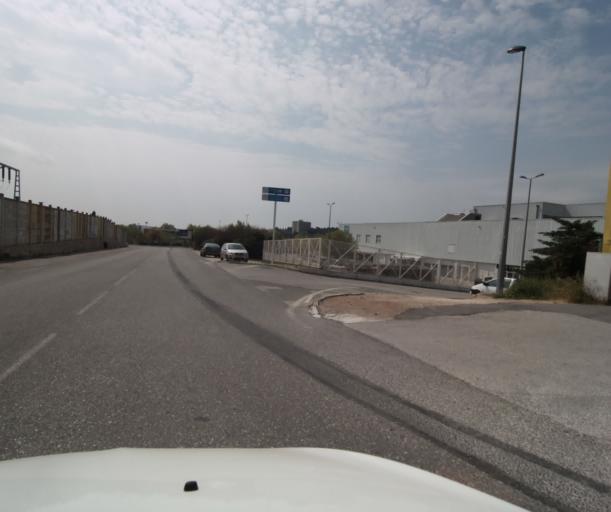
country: FR
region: Provence-Alpes-Cote d'Azur
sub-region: Departement du Var
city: La Garde
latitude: 43.1412
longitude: 6.0198
